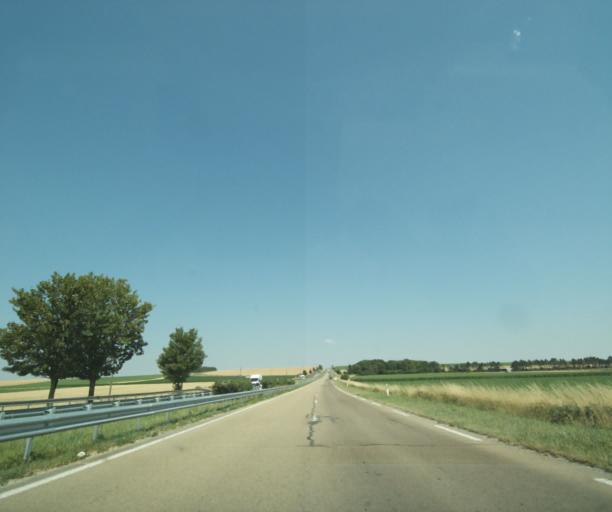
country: FR
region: Champagne-Ardenne
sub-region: Departement de la Marne
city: Fagnieres
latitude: 49.0423
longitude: 4.3095
